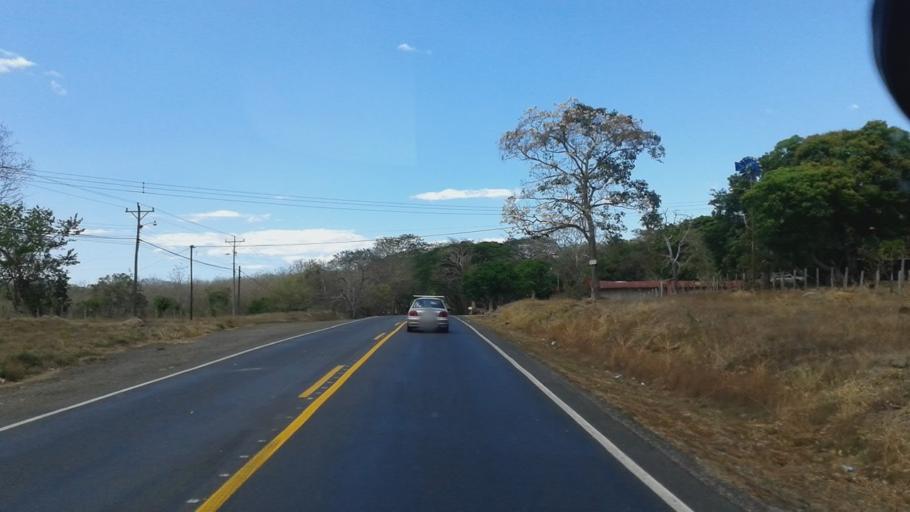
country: CR
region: Guanacaste
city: Juntas
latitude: 10.1452
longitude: -84.9097
